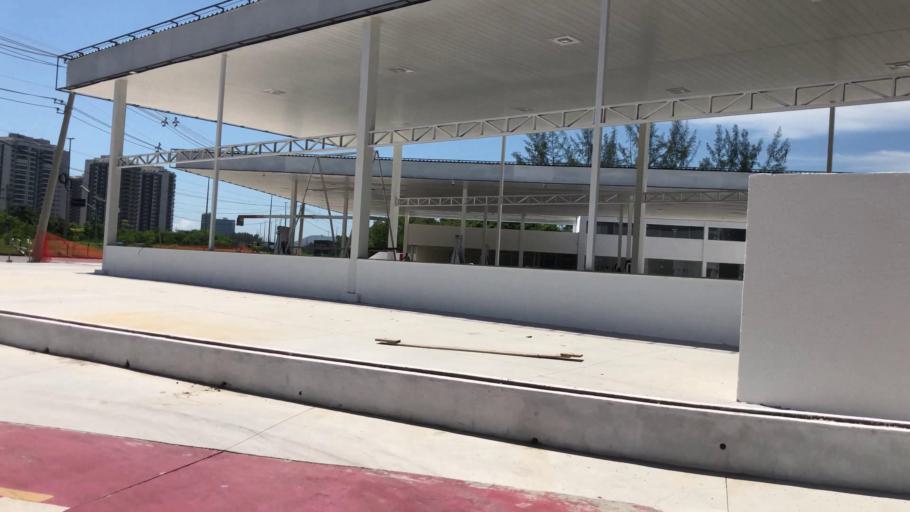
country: BR
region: Rio de Janeiro
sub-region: Nilopolis
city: Nilopolis
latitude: -22.9732
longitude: -43.3969
